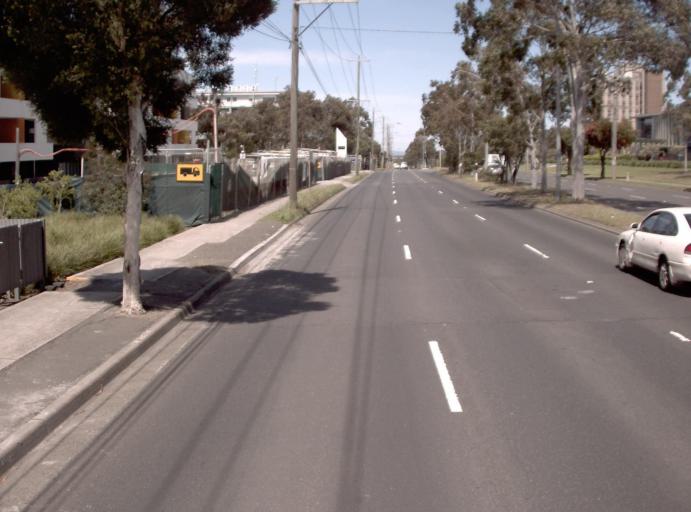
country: AU
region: Victoria
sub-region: Monash
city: Notting Hill
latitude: -37.9047
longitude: 145.1425
